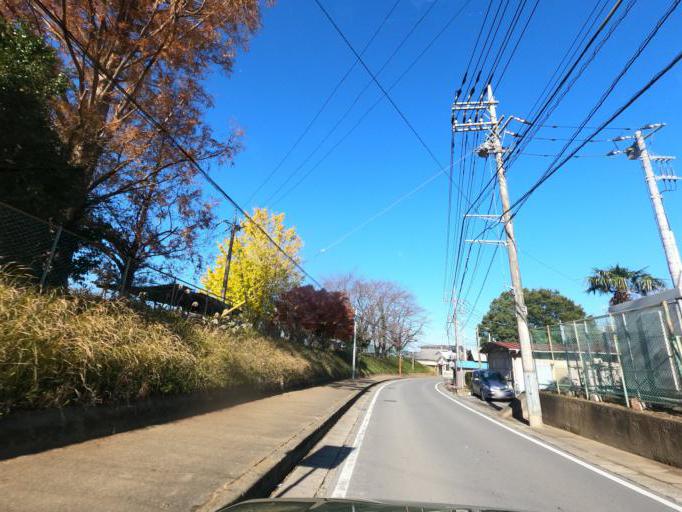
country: JP
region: Ibaraki
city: Mitsukaido
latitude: 36.0172
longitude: 139.9837
